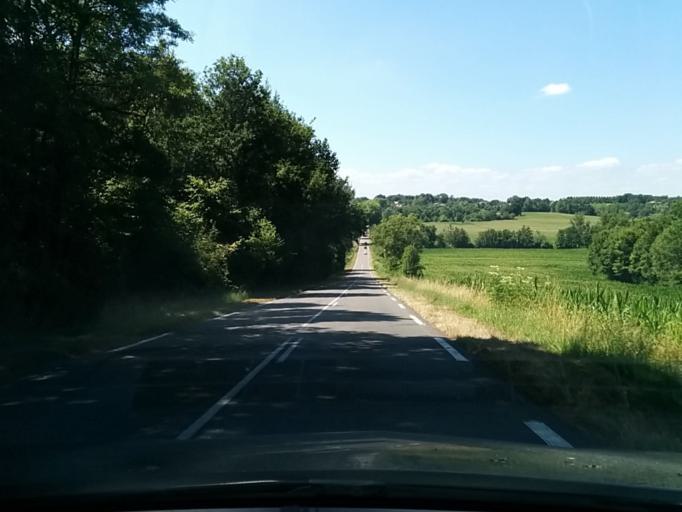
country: FR
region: Midi-Pyrenees
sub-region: Departement du Gers
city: Le Houga
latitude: 43.7706
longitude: -0.1262
